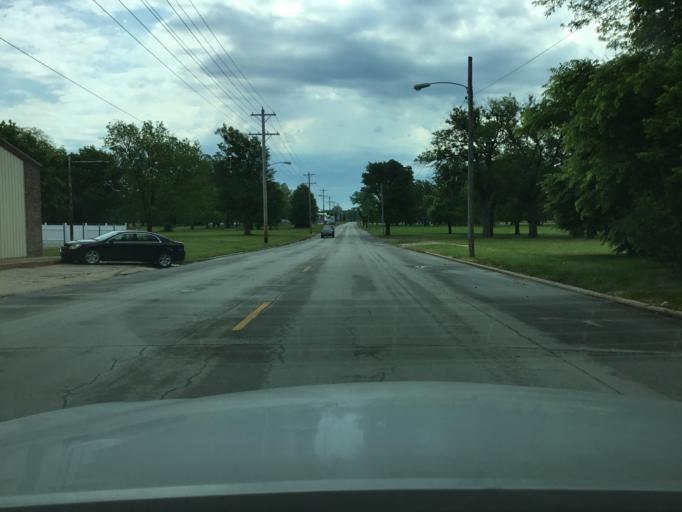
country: US
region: Kansas
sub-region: Montgomery County
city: Coffeyville
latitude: 37.0360
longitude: -95.6075
